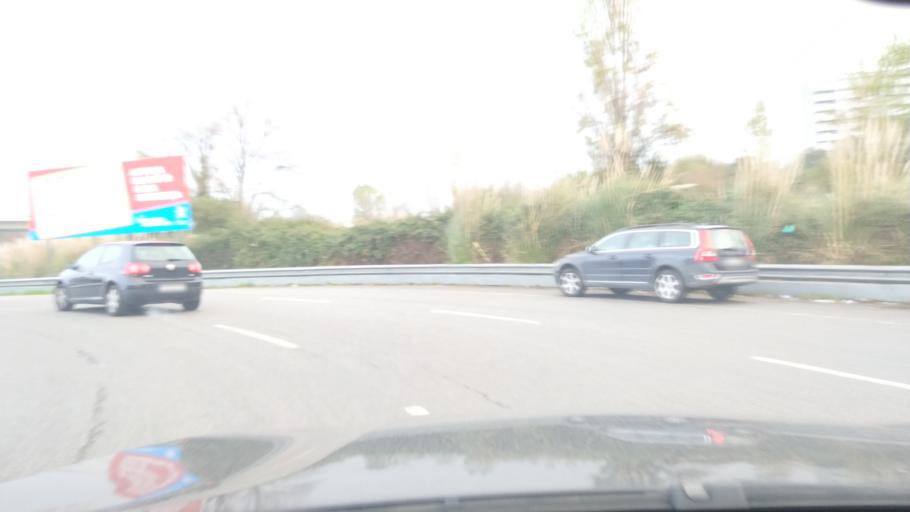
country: PT
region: Porto
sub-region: Porto
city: Porto
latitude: 41.1706
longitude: -8.6230
